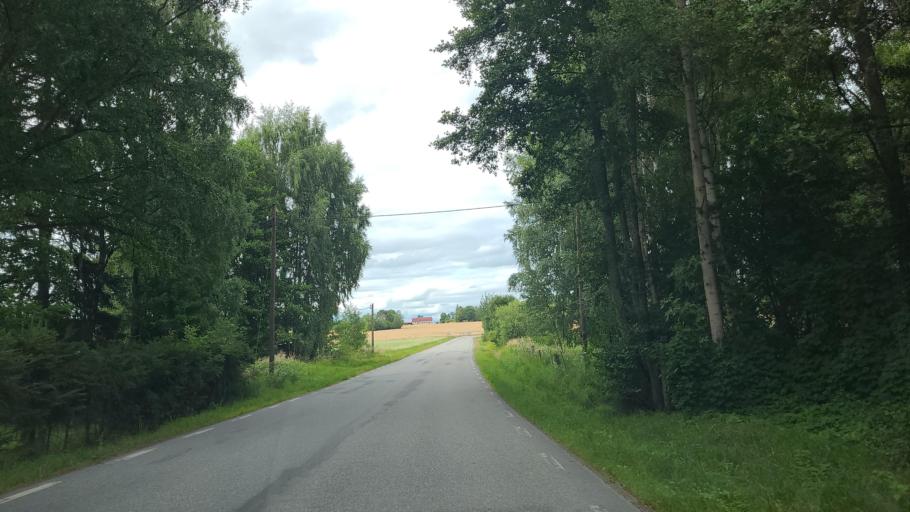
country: SE
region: Stockholm
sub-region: Upplands-Bro Kommun
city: Bro
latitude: 59.5018
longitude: 17.5657
